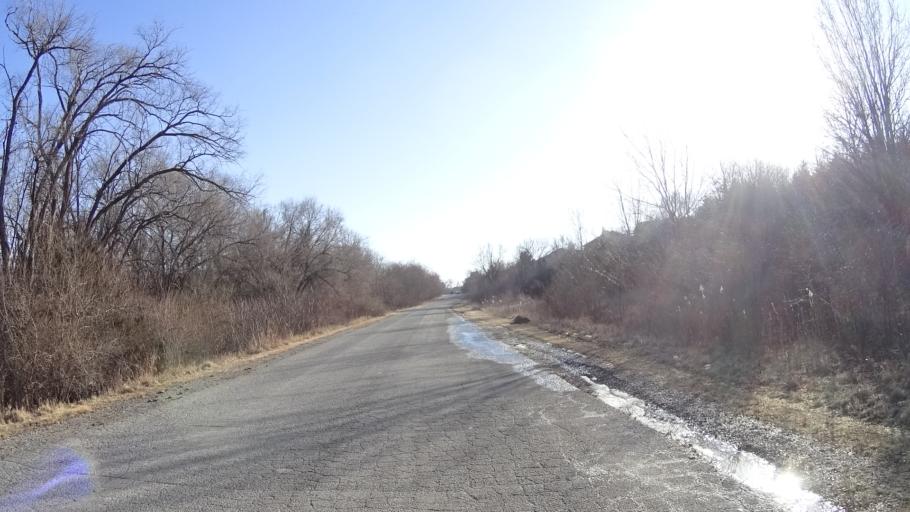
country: US
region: Nebraska
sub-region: Douglas County
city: Bennington
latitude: 41.3116
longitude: -96.1312
